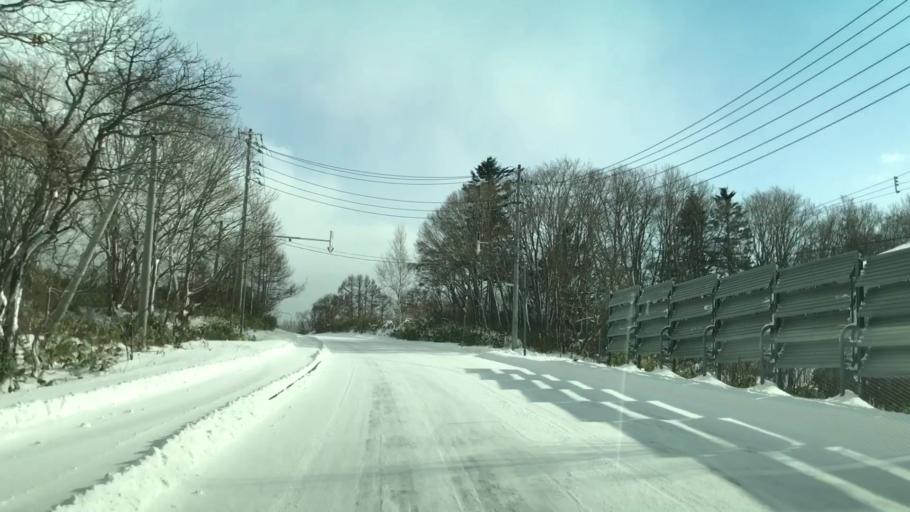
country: JP
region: Hokkaido
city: Yoichi
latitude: 43.3053
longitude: 140.5578
